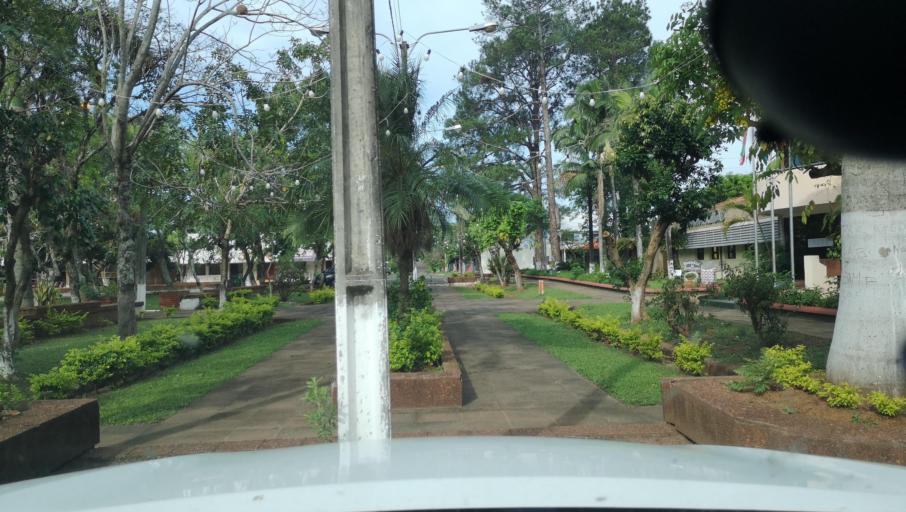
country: PY
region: Itapua
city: Carmen del Parana
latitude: -27.1623
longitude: -56.2395
